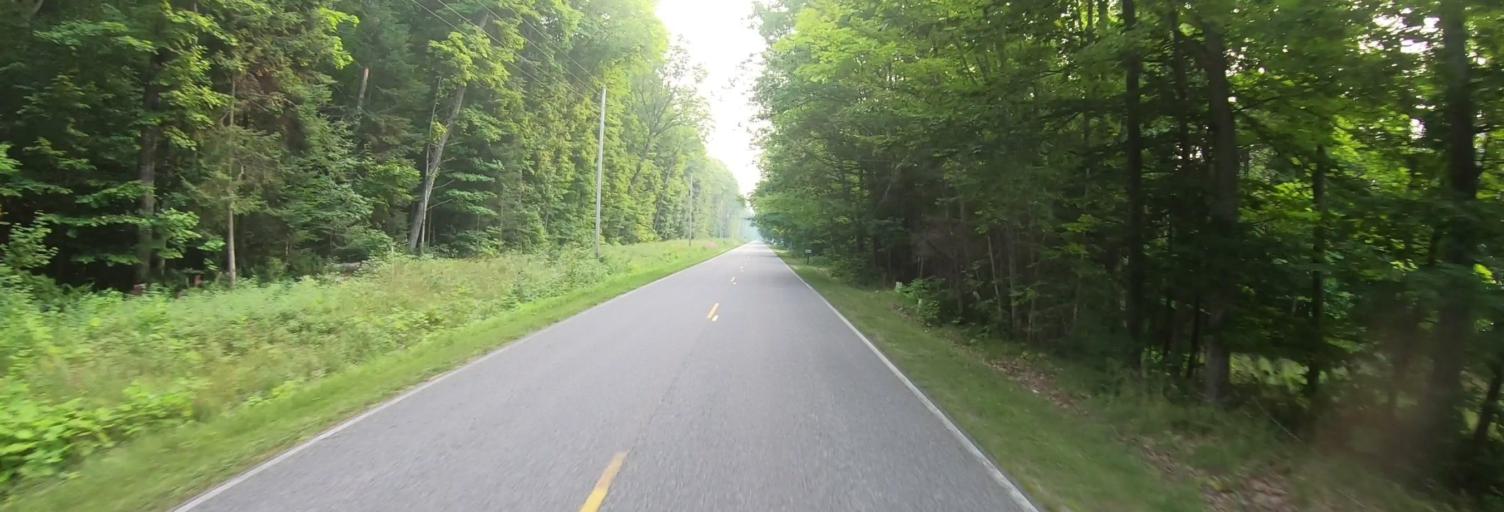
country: US
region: Michigan
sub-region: Chippewa County
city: Sault Ste. Marie
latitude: 46.4716
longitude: -84.7140
